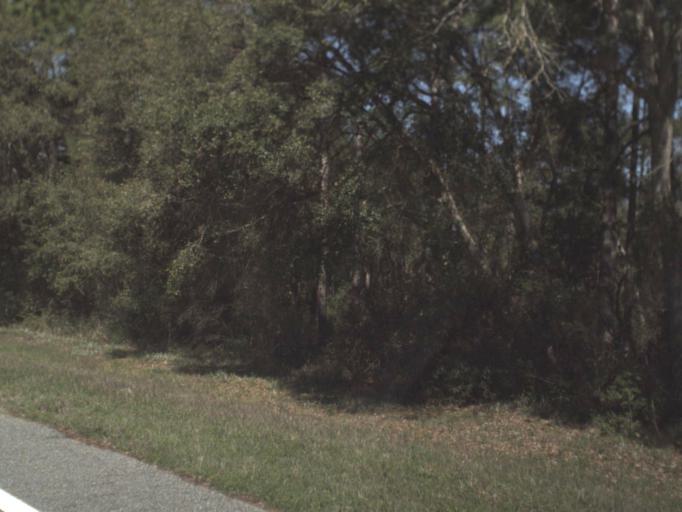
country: US
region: Florida
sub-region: Wakulla County
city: Crawfordville
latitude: 29.9460
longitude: -84.3861
